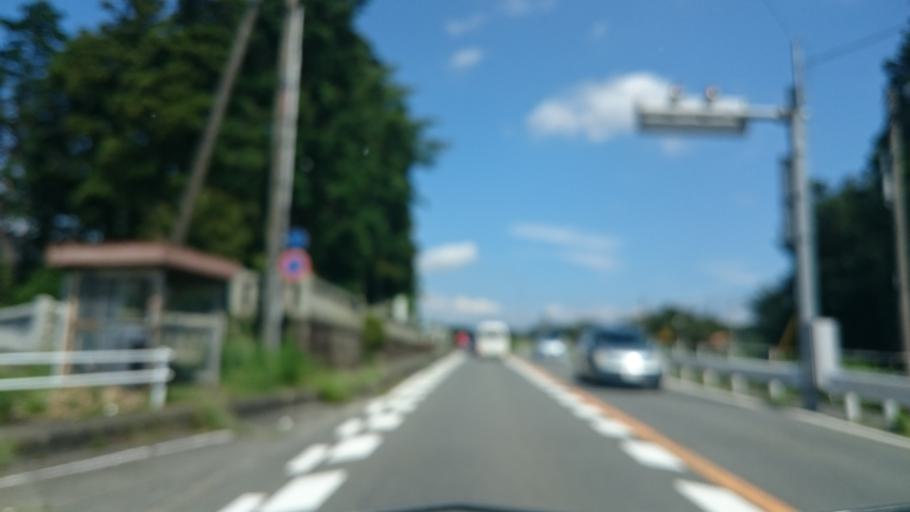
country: JP
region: Shizuoka
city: Gotemba
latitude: 35.2787
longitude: 138.9263
